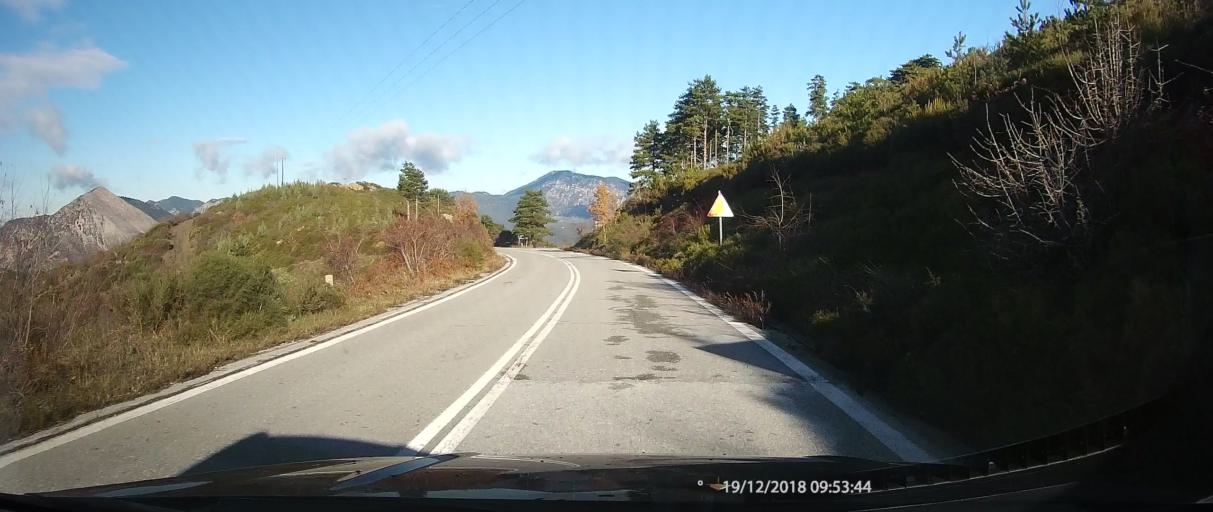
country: GR
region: Peloponnese
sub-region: Nomos Messinias
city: Paralia Vergas
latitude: 37.0752
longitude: 22.2522
